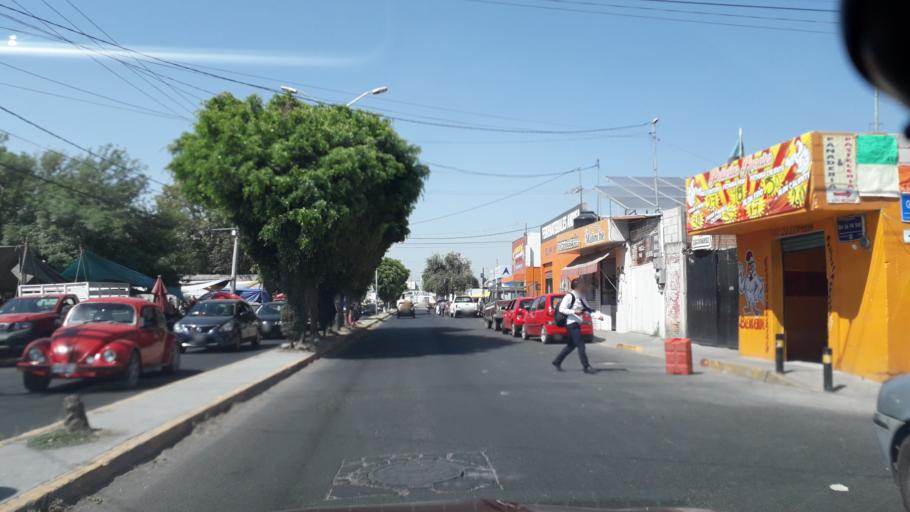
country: MX
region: Puebla
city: Puebla
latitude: 18.9910
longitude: -98.2140
